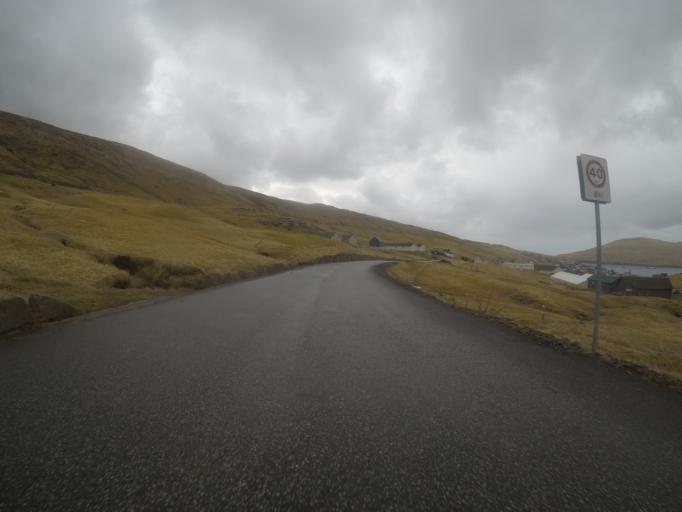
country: FO
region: Vagar
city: Midvagur
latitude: 62.0631
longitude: -7.1464
